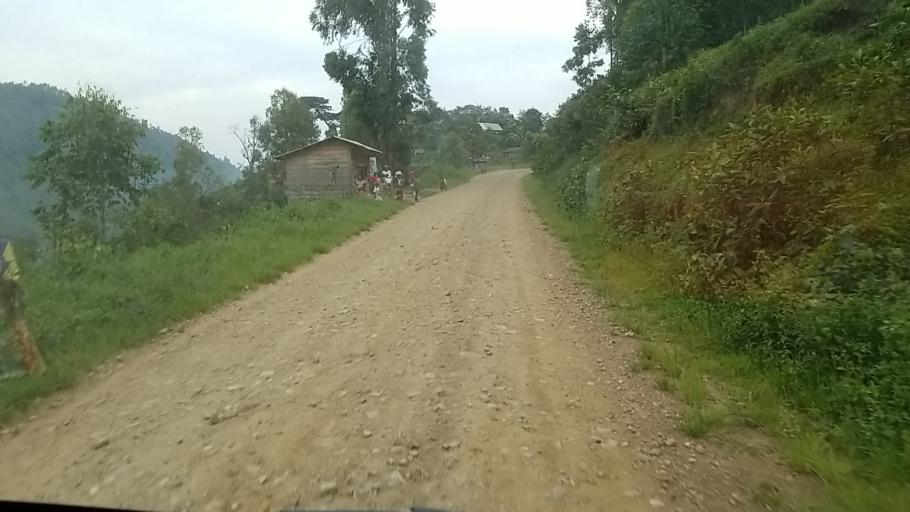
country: CD
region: Nord Kivu
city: Sake
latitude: -1.9552
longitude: 28.9210
